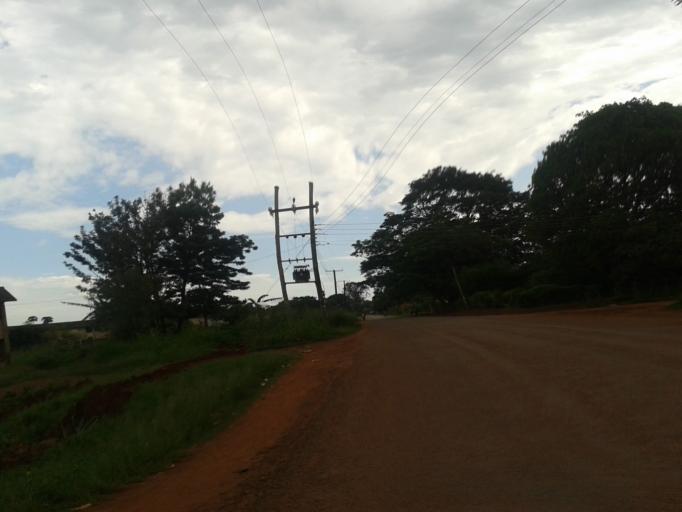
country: UG
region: Northern Region
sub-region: Gulu District
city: Gulu
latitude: 2.7844
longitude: 32.3073
